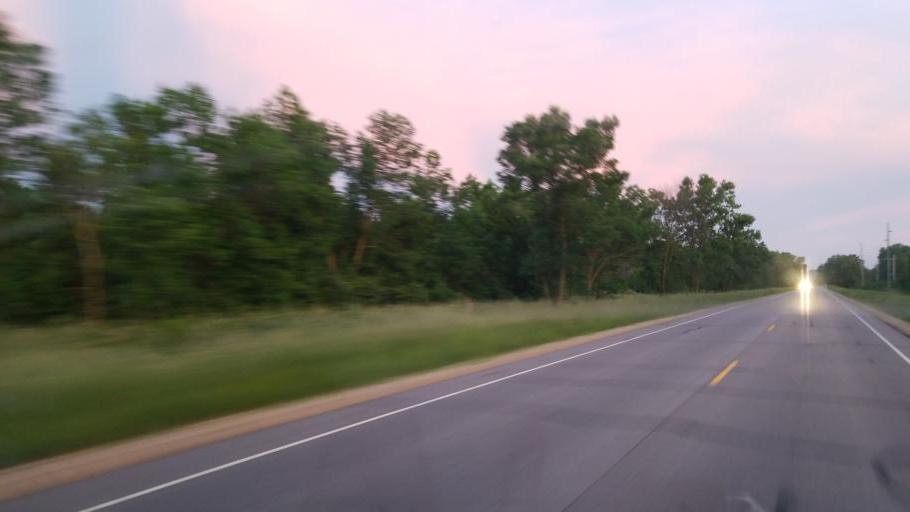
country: US
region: Wisconsin
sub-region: Juneau County
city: Elroy
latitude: 43.7102
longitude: -90.2662
